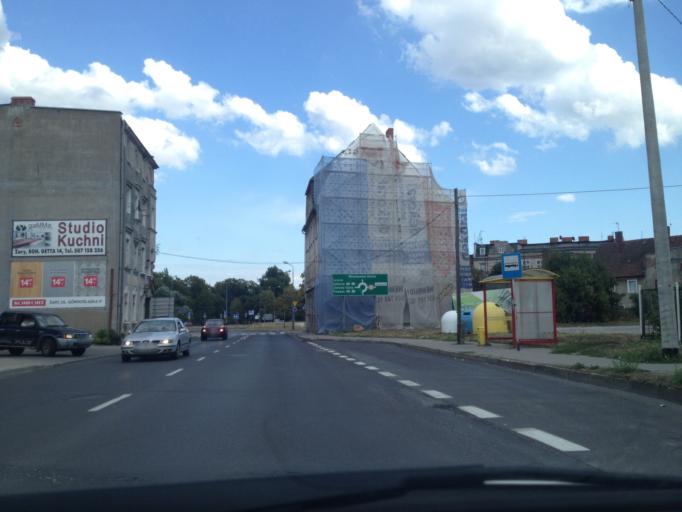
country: PL
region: Lubusz
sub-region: Powiat zarski
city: Zary
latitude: 51.6422
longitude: 15.1353
